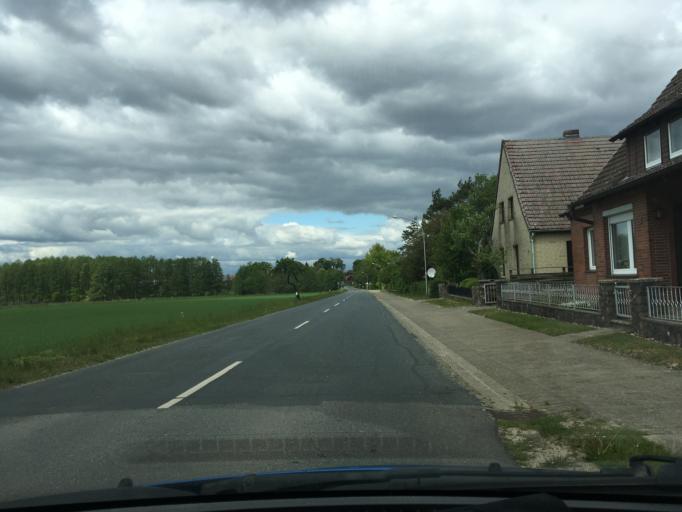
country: DE
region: Lower Saxony
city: Gerdau
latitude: 52.9177
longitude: 10.4173
